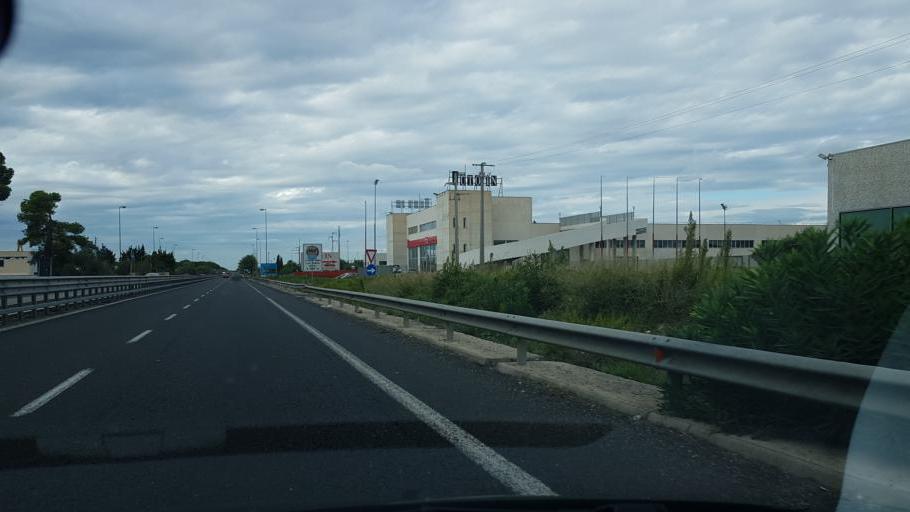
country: IT
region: Apulia
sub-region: Provincia di Lecce
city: Cavallino
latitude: 40.2868
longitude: 18.1993
